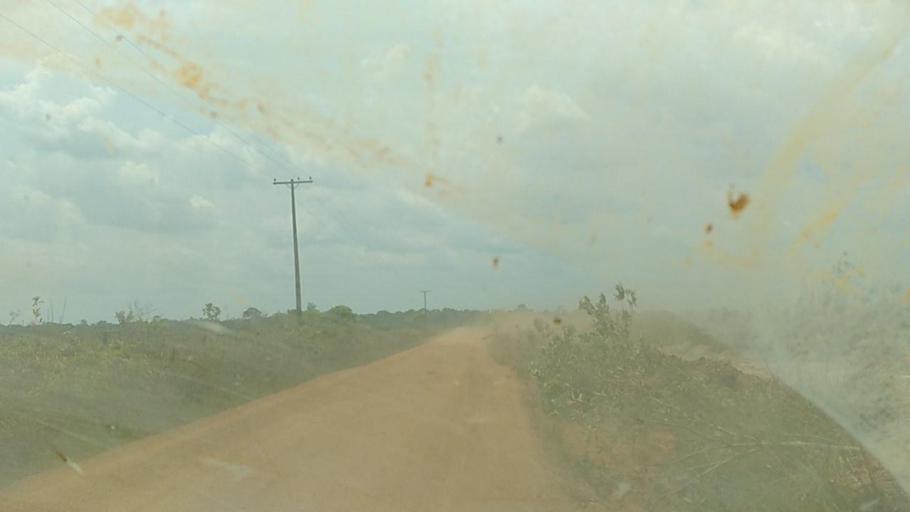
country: BR
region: Rondonia
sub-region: Porto Velho
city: Porto Velho
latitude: -8.9399
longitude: -64.3033
